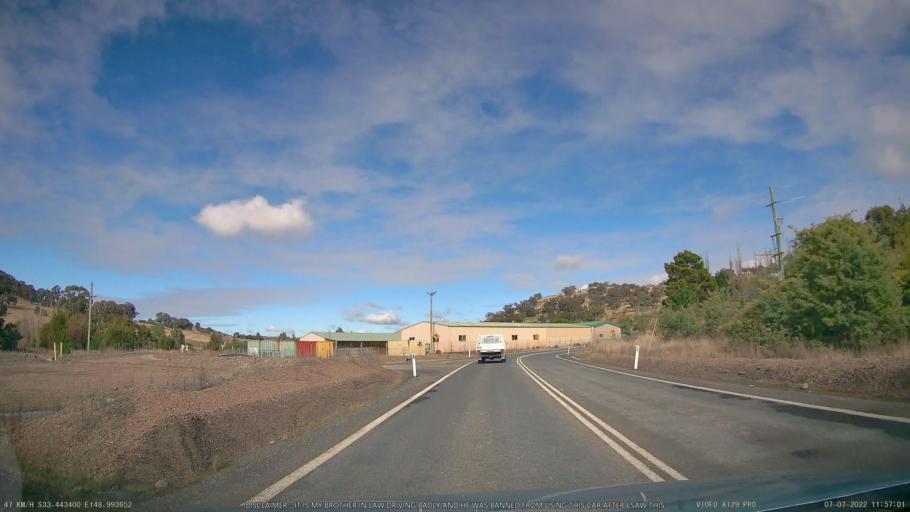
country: AU
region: New South Wales
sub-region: Orange Municipality
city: Orange
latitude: -33.4436
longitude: 148.9932
